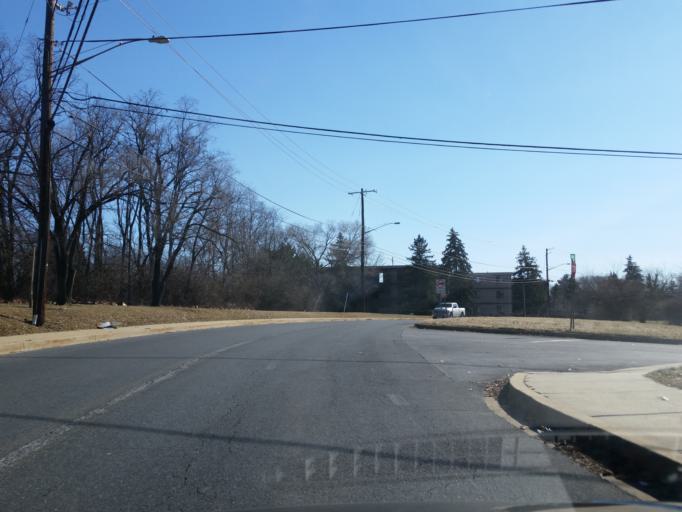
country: US
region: Maryland
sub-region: Montgomery County
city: Silver Spring
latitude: 38.9829
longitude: -77.0226
